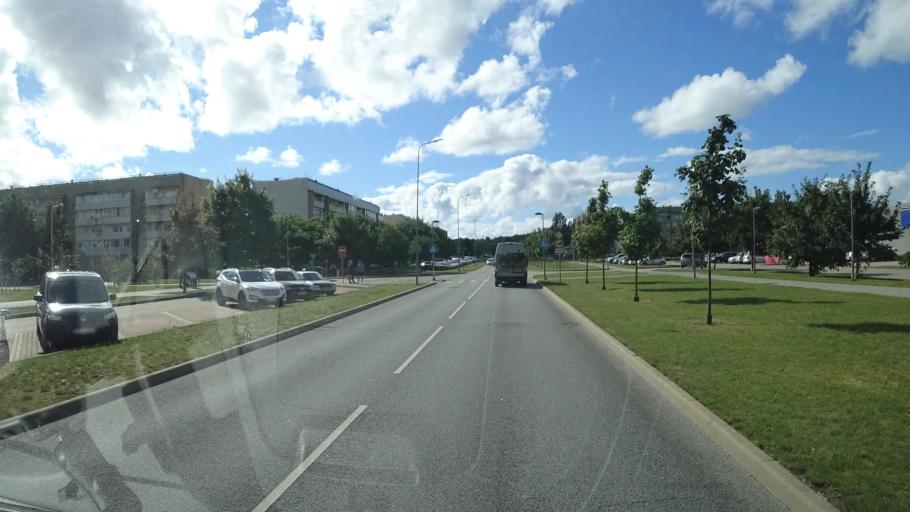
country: LV
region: Ventspils
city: Ventspils
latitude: 57.4071
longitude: 21.6003
